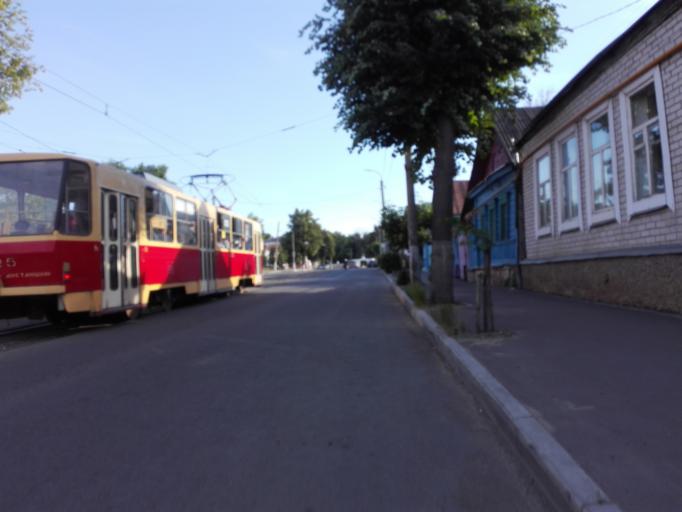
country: RU
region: Orjol
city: Orel
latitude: 52.9522
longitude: 36.0543
